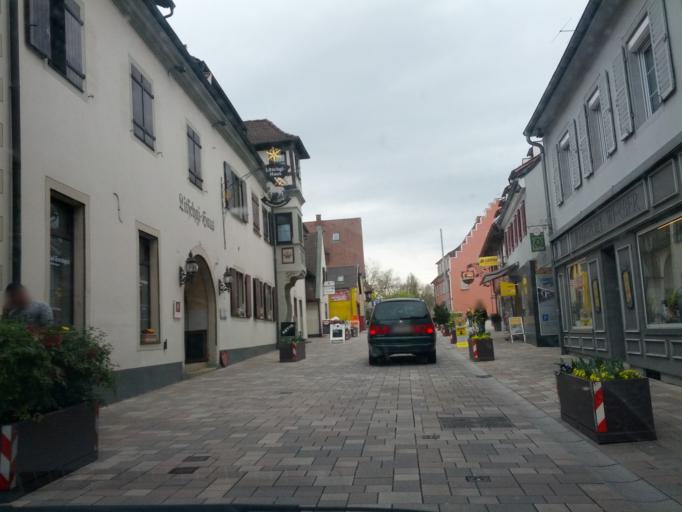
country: DE
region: Baden-Wuerttemberg
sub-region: Freiburg Region
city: Bad Krozingen
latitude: 47.9156
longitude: 7.6996
